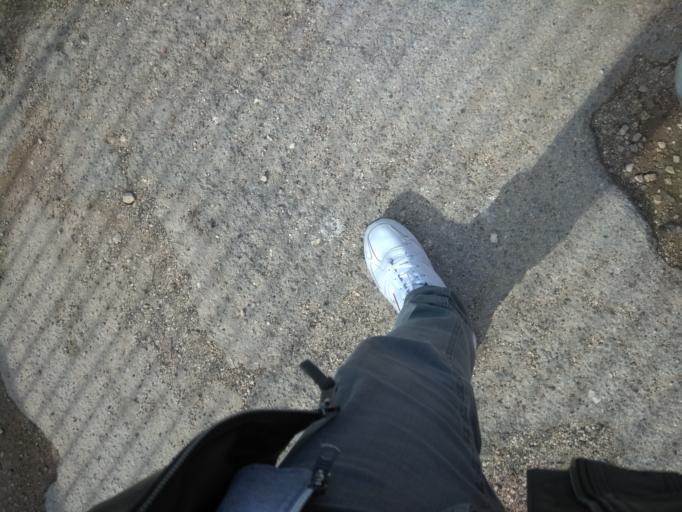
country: IT
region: Apulia
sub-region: Provincia di Bari
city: Bari
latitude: 41.1115
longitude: 16.9022
